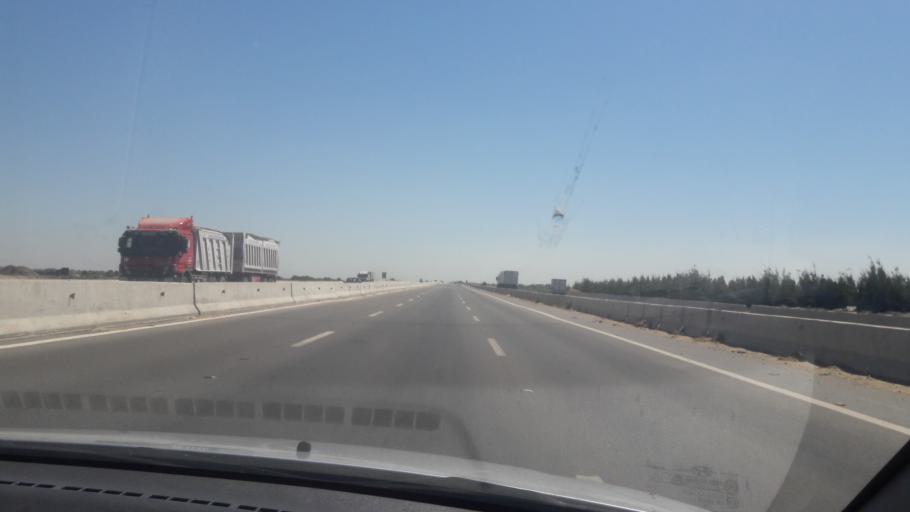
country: EG
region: Muhafazat ad Daqahliyah
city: Al Matariyah
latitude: 30.9087
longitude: 32.1865
